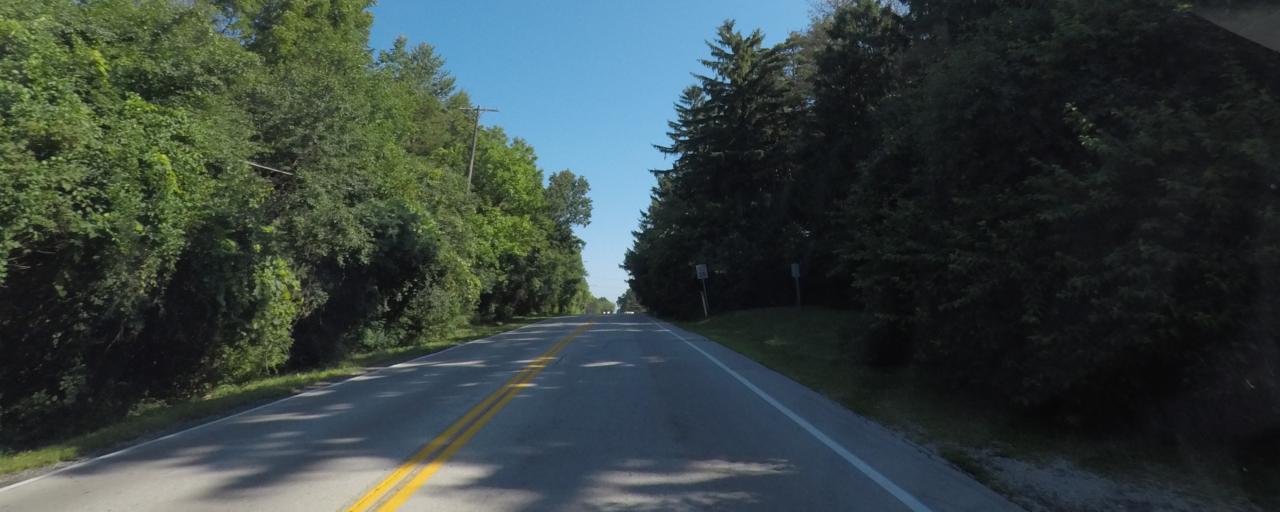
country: US
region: Wisconsin
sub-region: Waukesha County
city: Elm Grove
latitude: 43.0057
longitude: -88.0677
